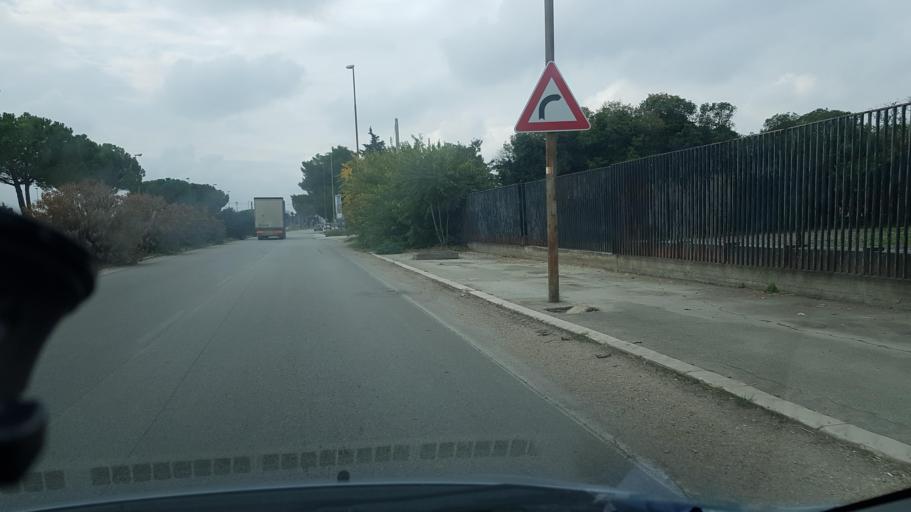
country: IT
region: Apulia
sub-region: Provincia di Foggia
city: Foggia
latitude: 41.4824
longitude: 15.5599
